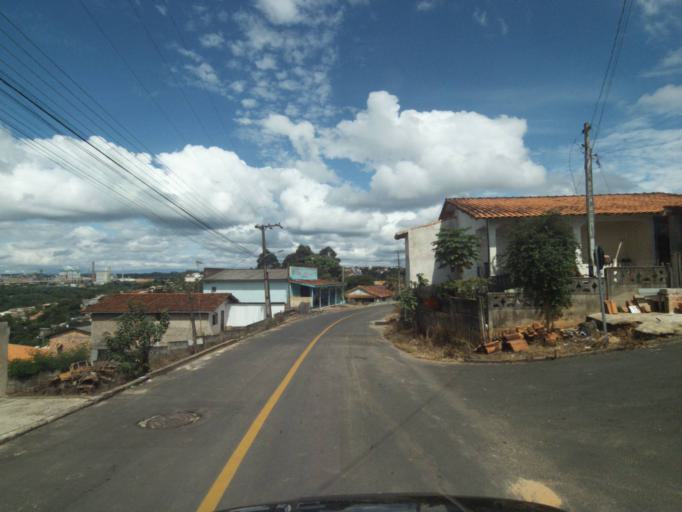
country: BR
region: Parana
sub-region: Telemaco Borba
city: Telemaco Borba
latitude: -24.3155
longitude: -50.6258
